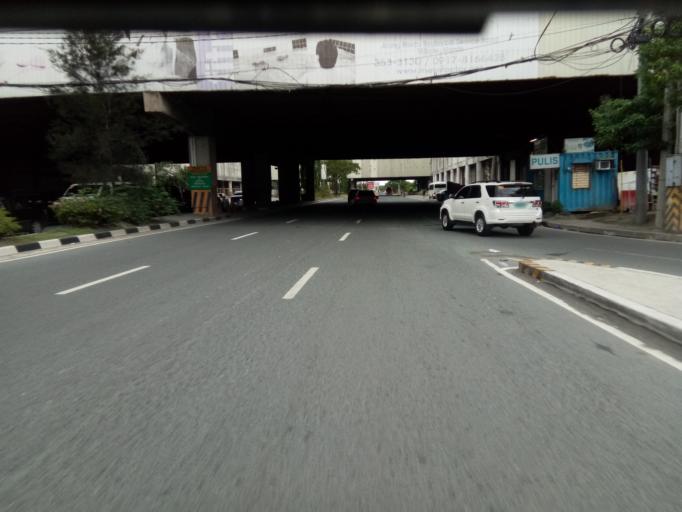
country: PH
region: Metro Manila
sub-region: Makati City
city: Makati City
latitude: 14.5171
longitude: 120.9905
